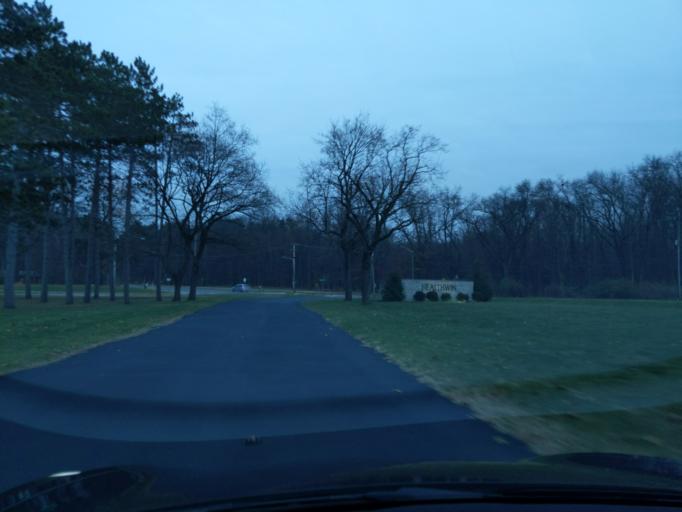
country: US
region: Indiana
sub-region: Saint Joseph County
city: Georgetown
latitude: 41.7313
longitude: -86.2664
